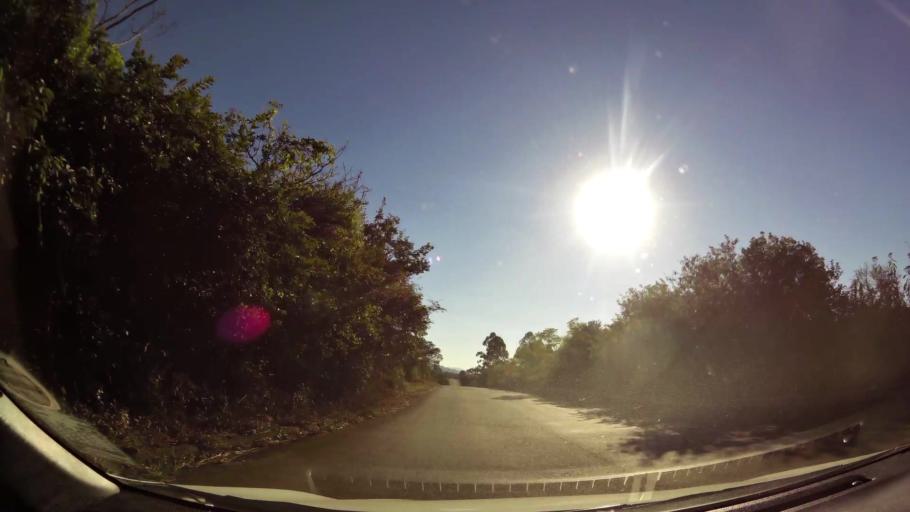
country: ZA
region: Limpopo
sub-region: Mopani District Municipality
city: Tzaneen
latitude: -23.9301
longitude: 30.0408
